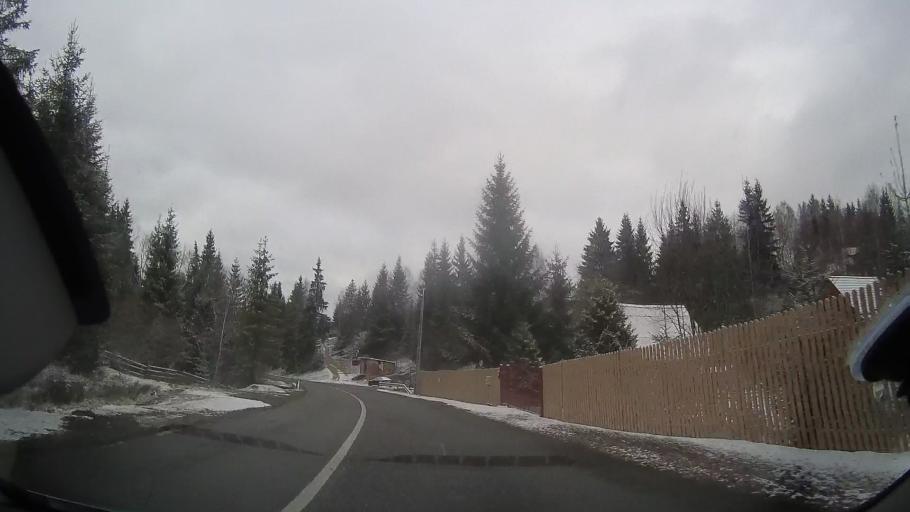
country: RO
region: Cluj
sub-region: Comuna Calatele
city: Calatele
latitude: 46.7158
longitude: 23.0443
